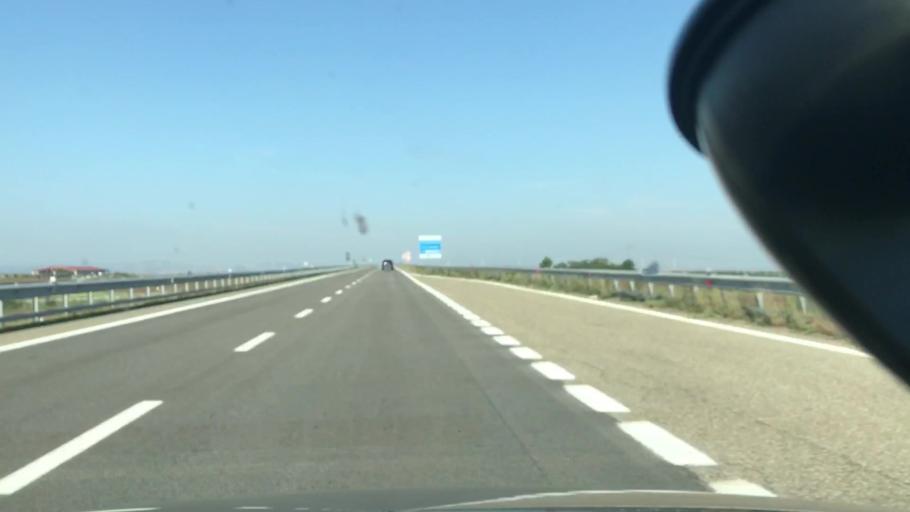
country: IT
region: Basilicate
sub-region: Provincia di Potenza
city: Montemilone
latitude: 40.9919
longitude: 15.8947
